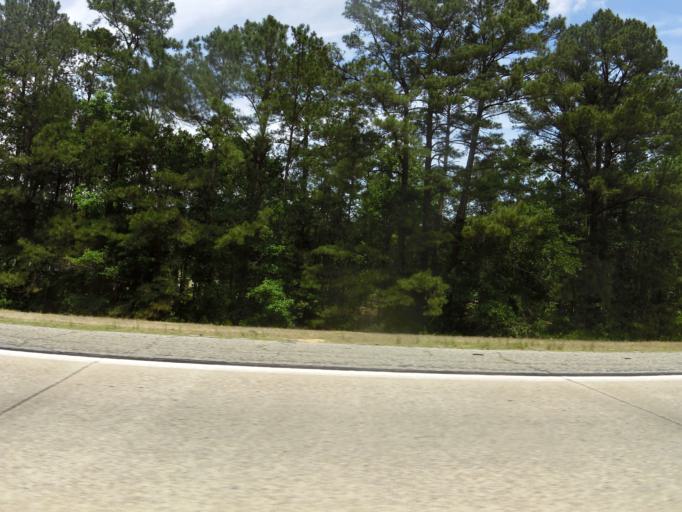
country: US
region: Georgia
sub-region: Bulloch County
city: Brooklet
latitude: 32.2525
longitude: -81.6986
